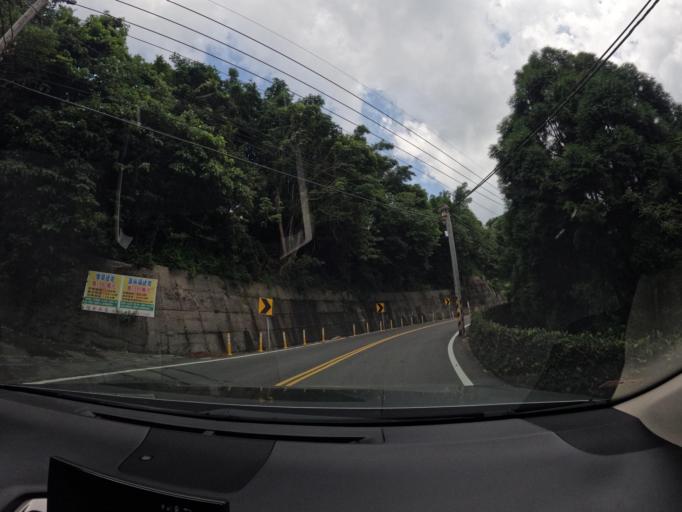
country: TW
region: Taiwan
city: Fengyuan
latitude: 24.3834
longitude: 120.8099
